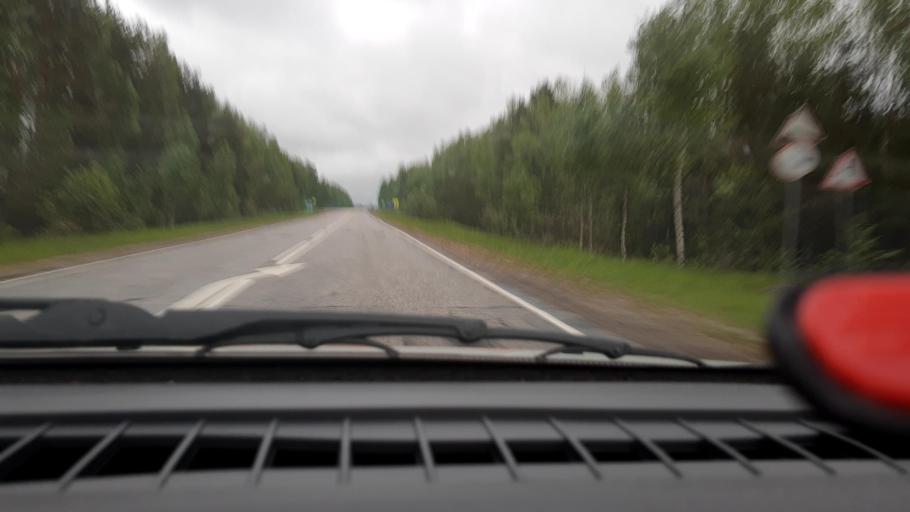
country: RU
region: Nizjnij Novgorod
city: Krasnyye Baki
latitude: 57.1870
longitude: 45.4011
